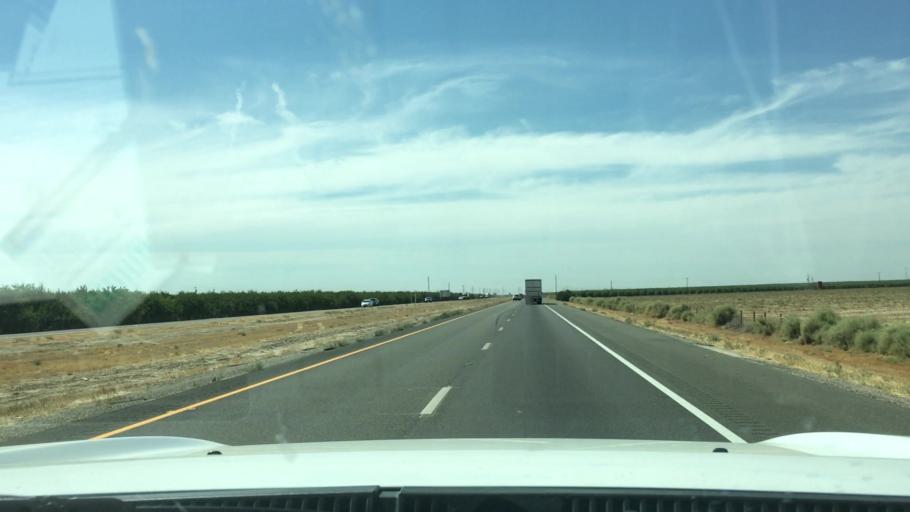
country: US
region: California
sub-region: Kern County
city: Buttonwillow
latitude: 35.4592
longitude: -119.4795
